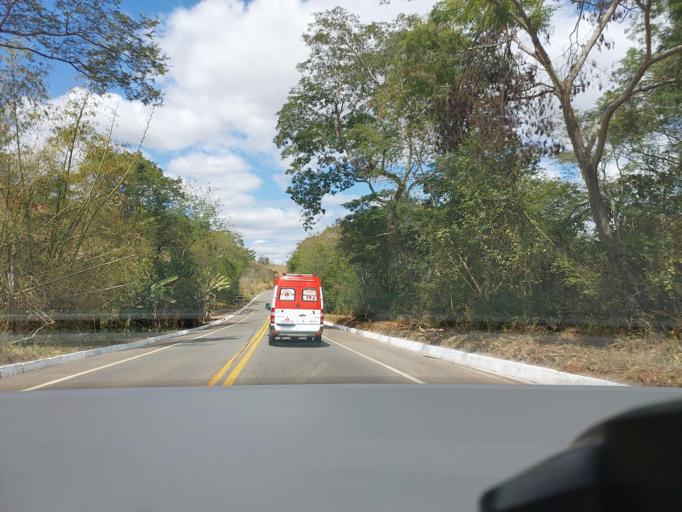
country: BR
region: Minas Gerais
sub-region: Muriae
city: Muriae
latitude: -21.1313
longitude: -42.3175
